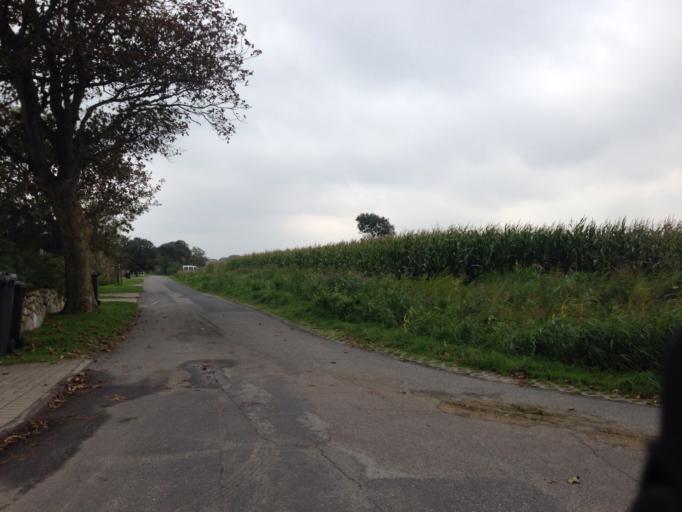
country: DE
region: Schleswig-Holstein
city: Alkersum
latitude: 54.7068
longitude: 8.5036
